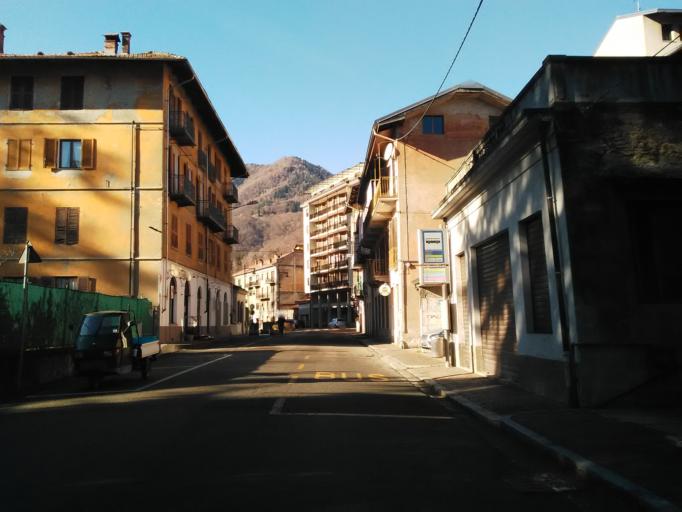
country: IT
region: Piedmont
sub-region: Provincia di Biella
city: Coggiola
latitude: 45.6850
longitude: 8.1850
